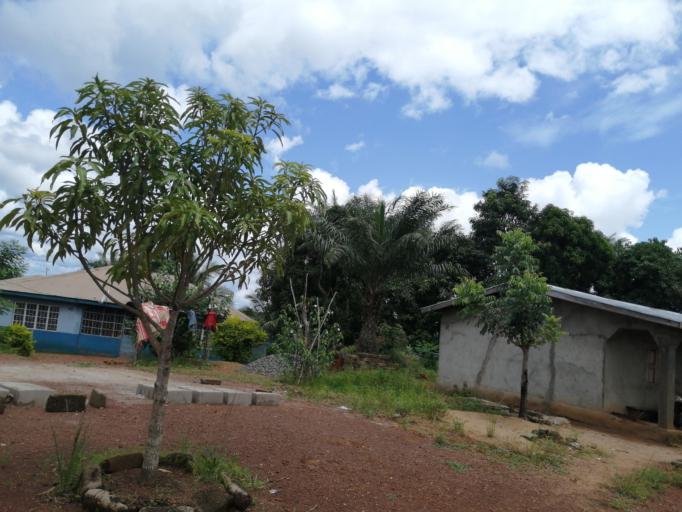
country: SL
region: Northern Province
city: Port Loko
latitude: 8.7810
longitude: -12.7986
